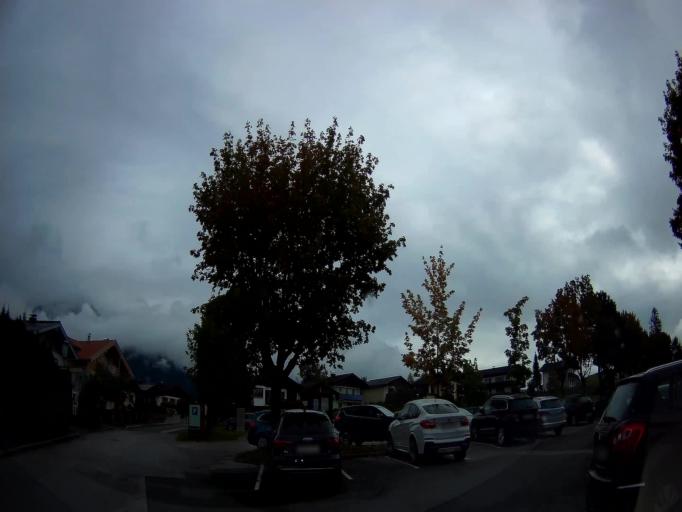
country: AT
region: Salzburg
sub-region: Politischer Bezirk Zell am See
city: Saalfelden am Steinernen Meer
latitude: 47.4207
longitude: 12.8476
